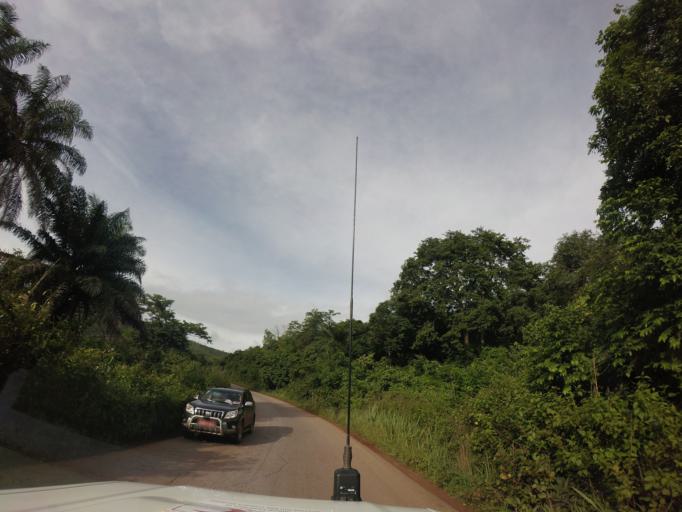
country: GN
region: Kindia
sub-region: Kindia
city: Kindia
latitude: 9.9064
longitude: -12.9966
